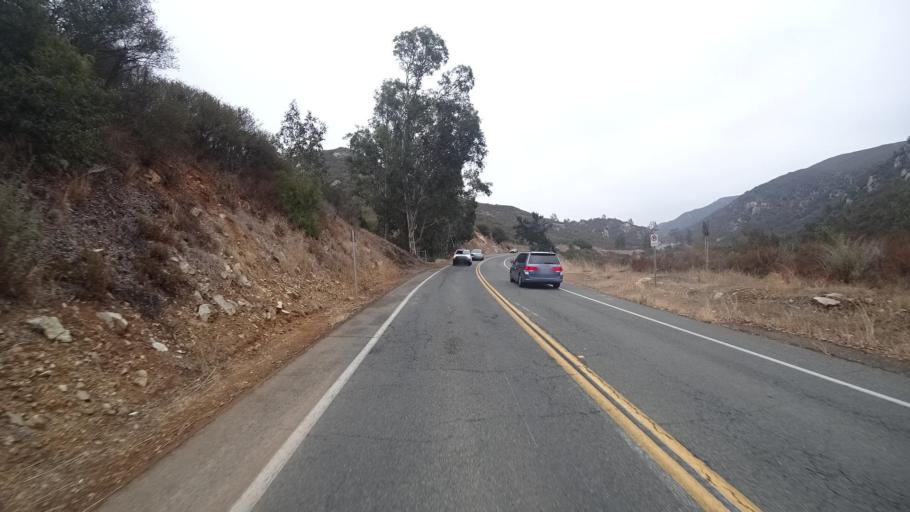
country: US
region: California
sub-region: San Diego County
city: San Marcos
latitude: 33.0857
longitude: -117.1535
